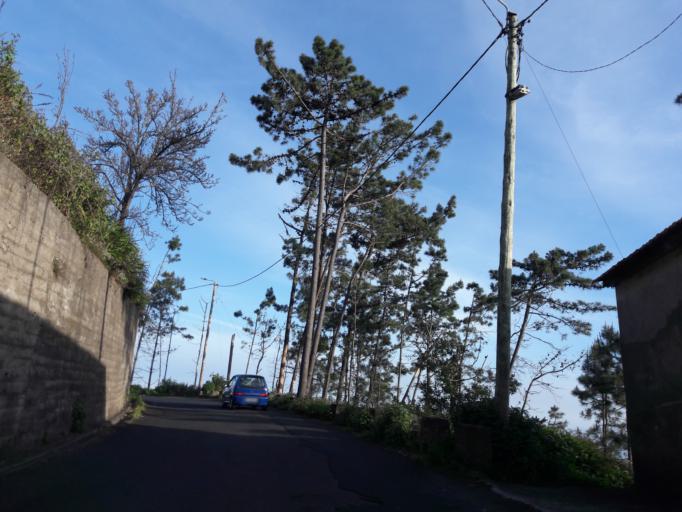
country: PT
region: Madeira
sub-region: Santa Cruz
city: Camacha
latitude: 32.6659
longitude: -16.8474
